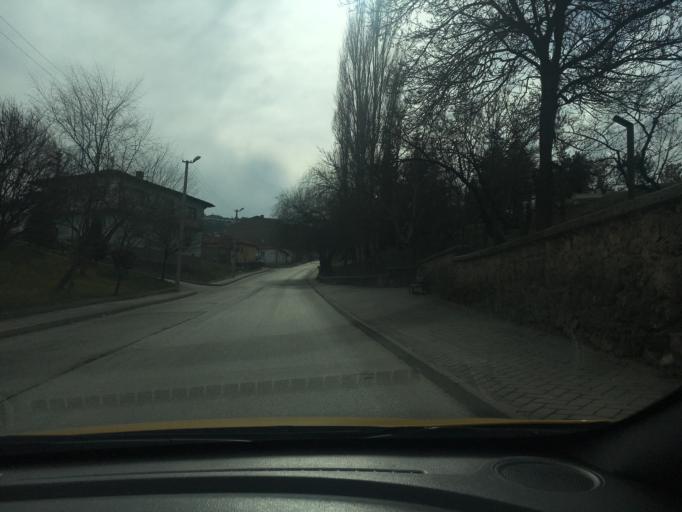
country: TR
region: Eskisehir
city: Eskisehir
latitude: 39.7616
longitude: 30.5287
